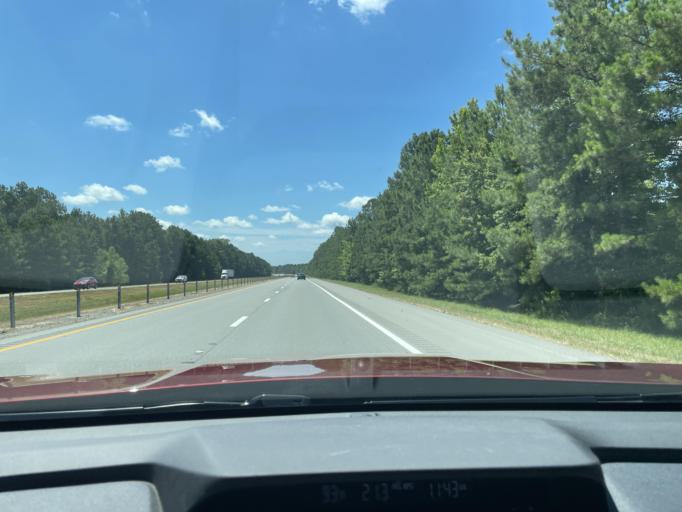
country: US
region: Arkansas
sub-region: Jefferson County
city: White Hall
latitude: 34.3194
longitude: -92.1496
